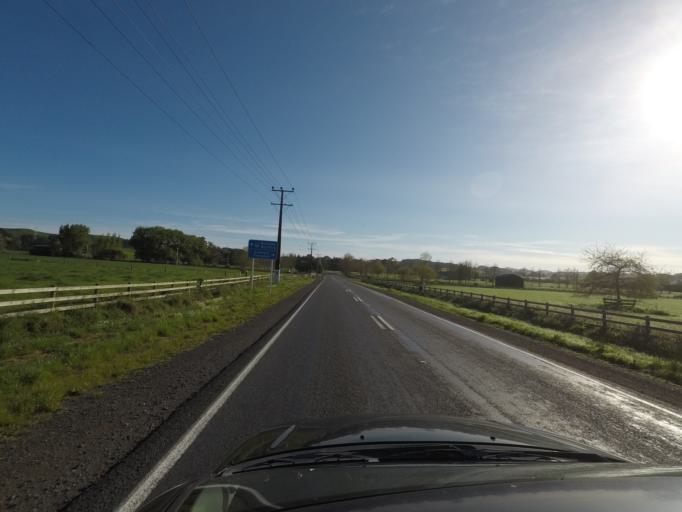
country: NZ
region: Auckland
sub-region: Auckland
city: Red Hill
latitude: -37.0057
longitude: 174.9551
